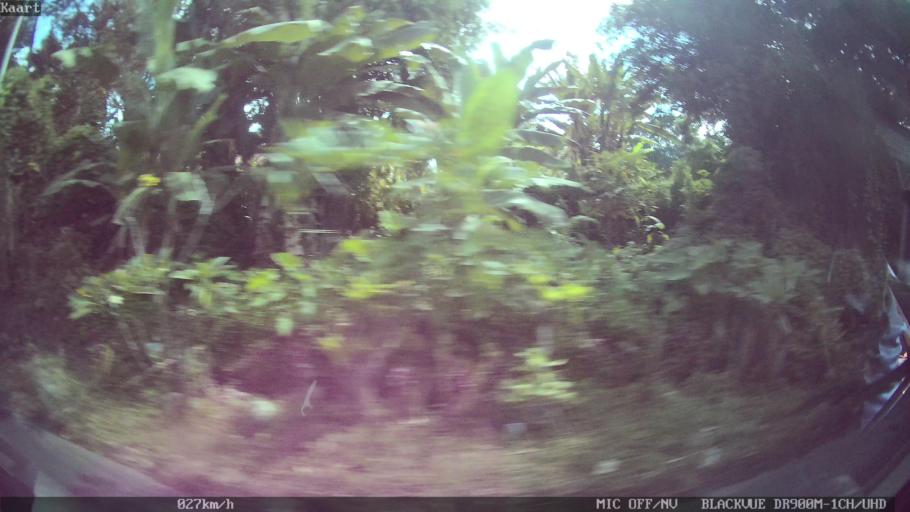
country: ID
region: Bali
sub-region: Kabupaten Gianyar
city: Ubud
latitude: -8.5288
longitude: 115.2997
